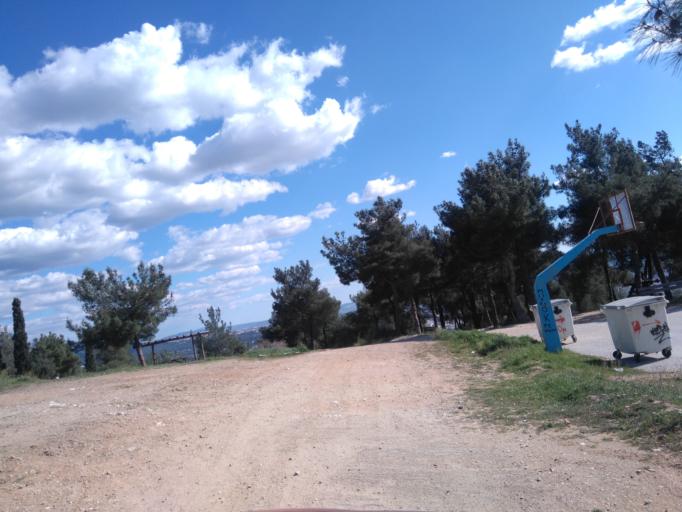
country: GR
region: Central Macedonia
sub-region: Nomos Thessalonikis
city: Agios Pavlos
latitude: 40.6369
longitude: 22.9784
